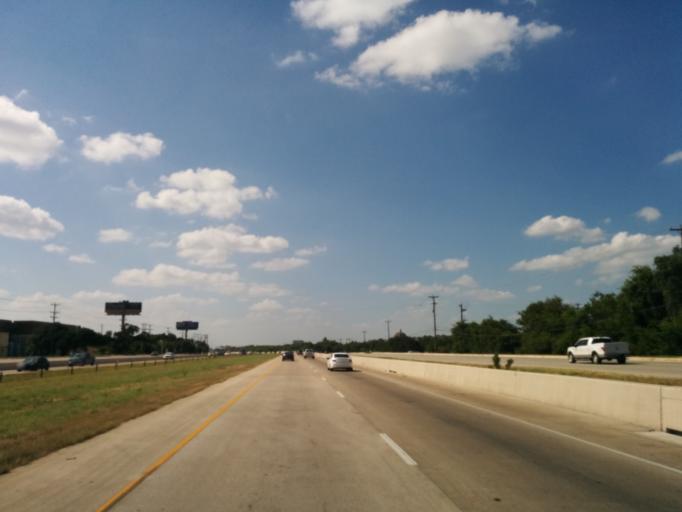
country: US
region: Texas
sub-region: Bexar County
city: Cross Mountain
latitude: 29.6317
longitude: -98.6122
